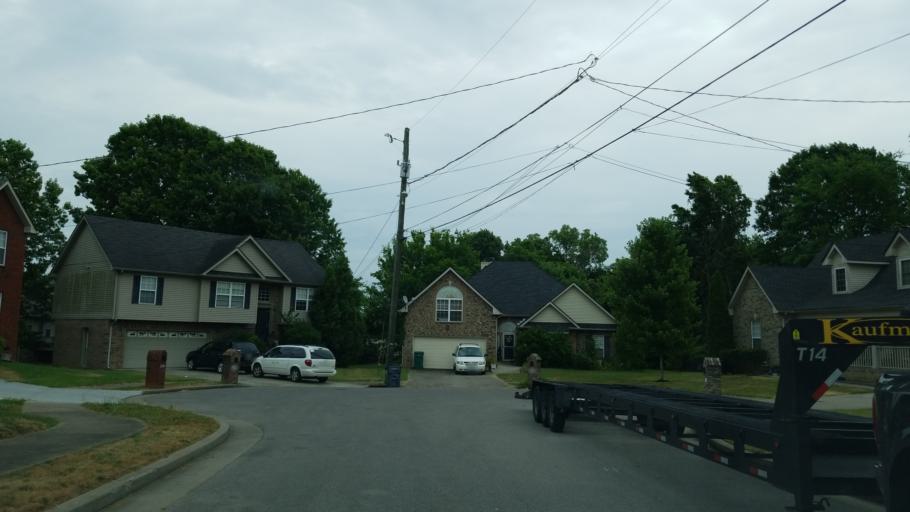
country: US
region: Tennessee
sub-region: Rutherford County
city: La Vergne
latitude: 36.0594
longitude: -86.5889
